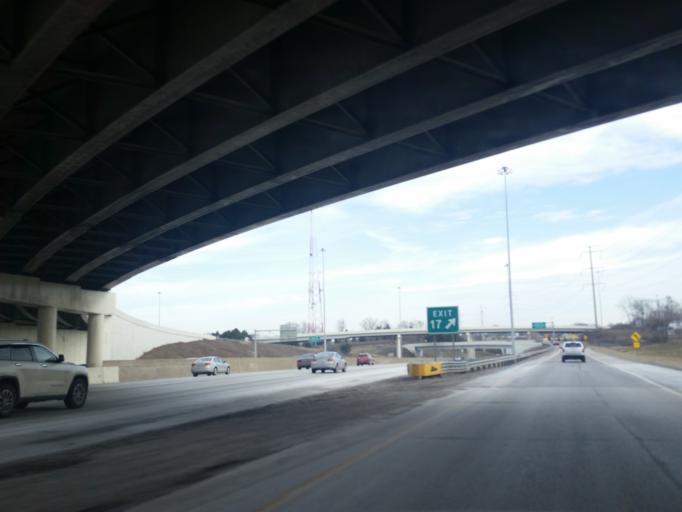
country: US
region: Ohio
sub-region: Cuyahoga County
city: Brooklyn Heights
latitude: 41.4209
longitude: -81.6902
